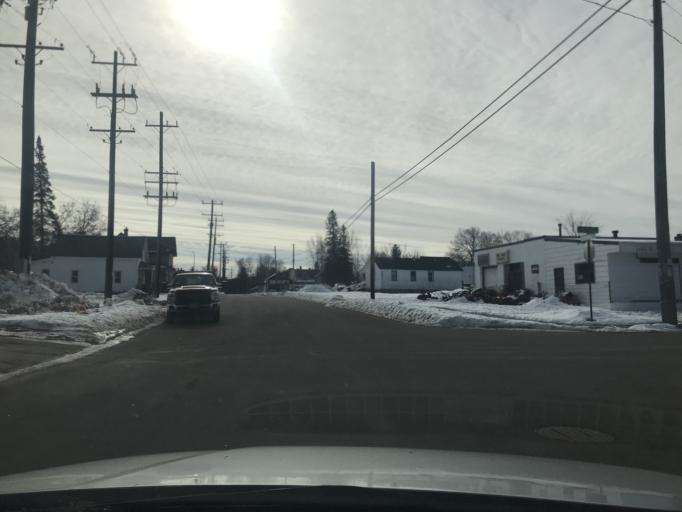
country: US
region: Wisconsin
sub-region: Oconto County
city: Gillett
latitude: 44.8921
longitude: -88.3024
